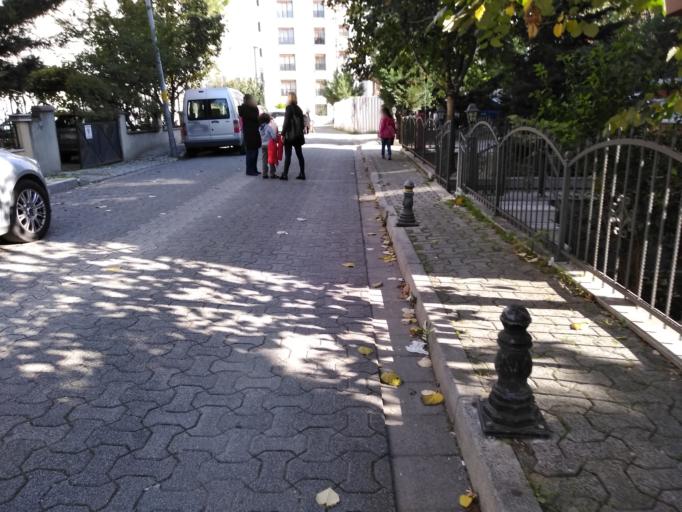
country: TR
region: Istanbul
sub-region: Atasehir
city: Atasehir
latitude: 40.9812
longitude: 29.1146
